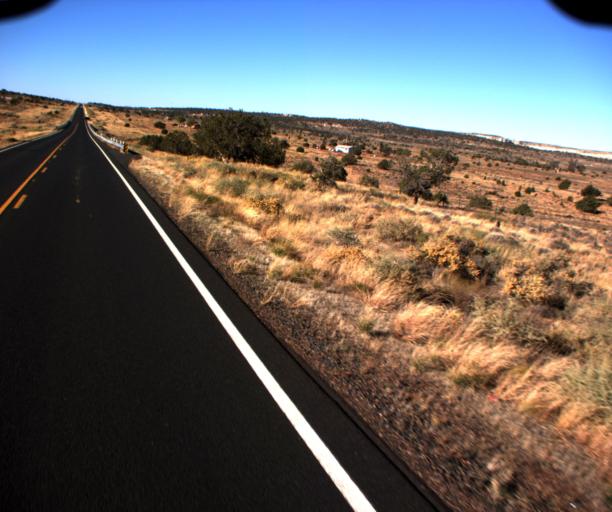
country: US
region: Arizona
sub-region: Apache County
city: Ganado
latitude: 35.7769
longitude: -109.7315
